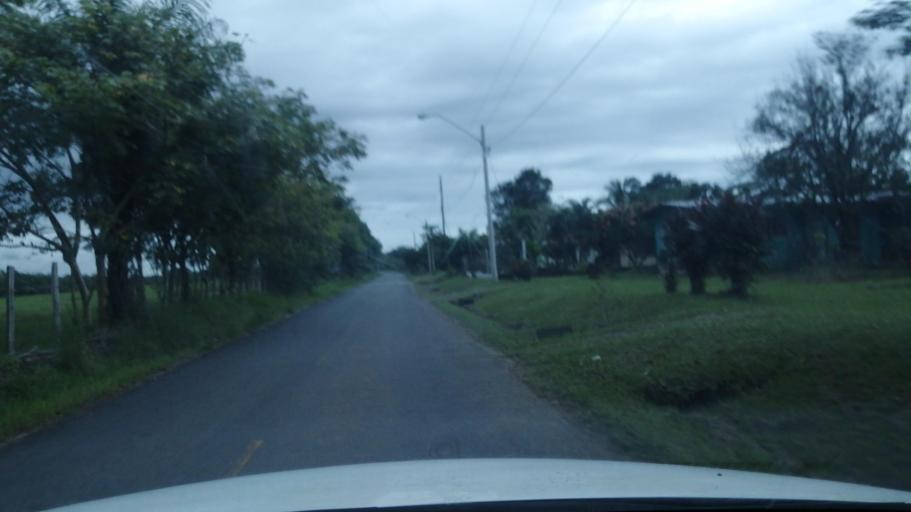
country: PA
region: Chiriqui
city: Alanje
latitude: 8.4100
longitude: -82.5018
